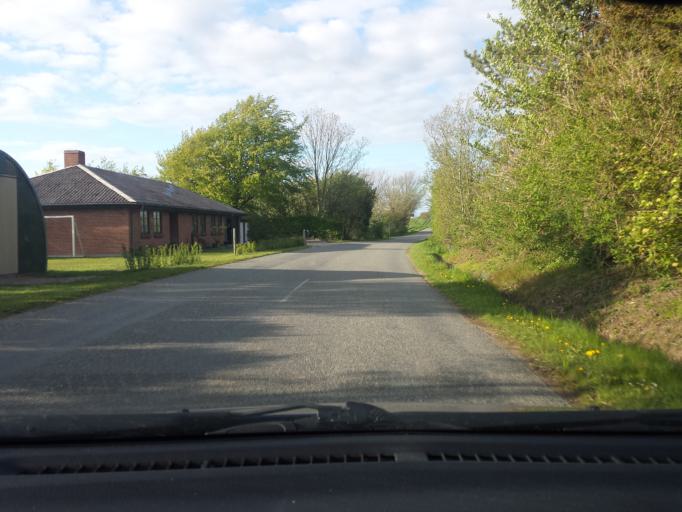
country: DK
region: South Denmark
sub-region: Langeland Kommune
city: Rudkobing
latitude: 54.8810
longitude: 10.7451
